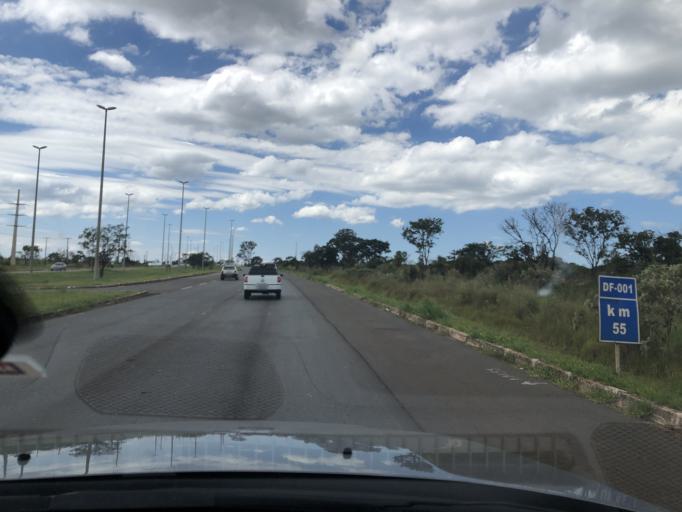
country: BR
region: Federal District
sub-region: Brasilia
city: Brasilia
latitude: -15.9784
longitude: -48.0013
